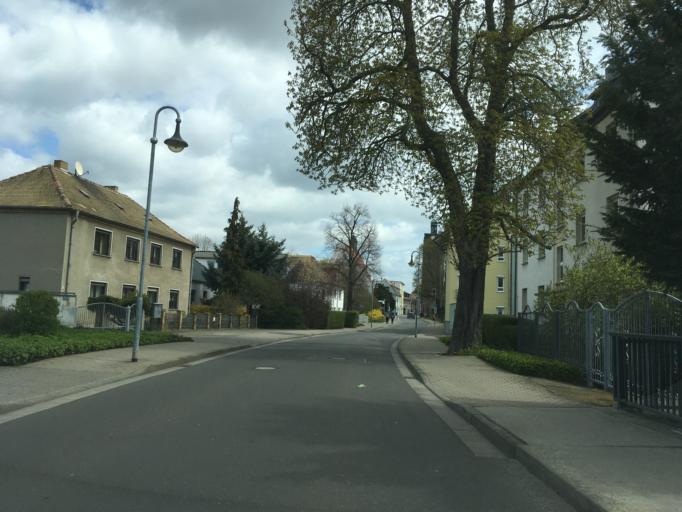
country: DE
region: Saxony
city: Delitzsch
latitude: 51.5215
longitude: 12.3259
